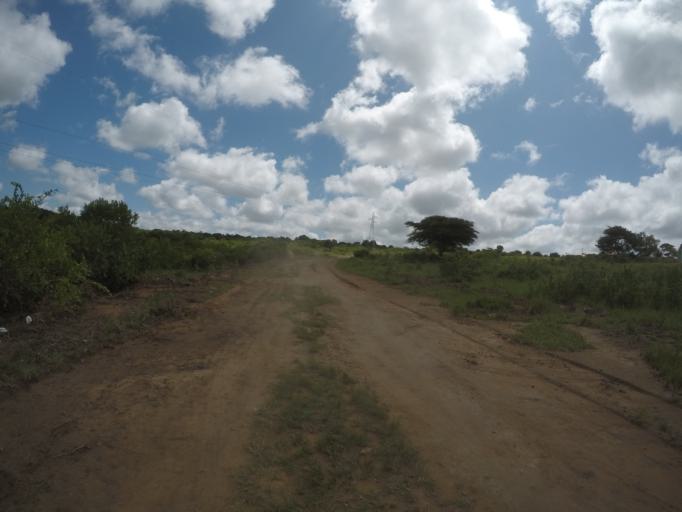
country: ZA
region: KwaZulu-Natal
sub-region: uThungulu District Municipality
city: Empangeni
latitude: -28.5874
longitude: 31.8370
